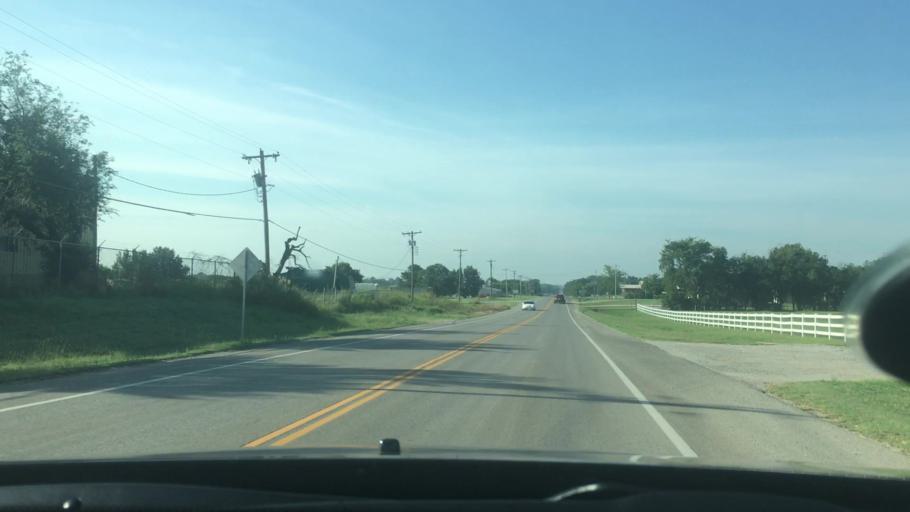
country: US
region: Oklahoma
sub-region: Garvin County
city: Pauls Valley
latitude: 34.7094
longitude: -97.2129
